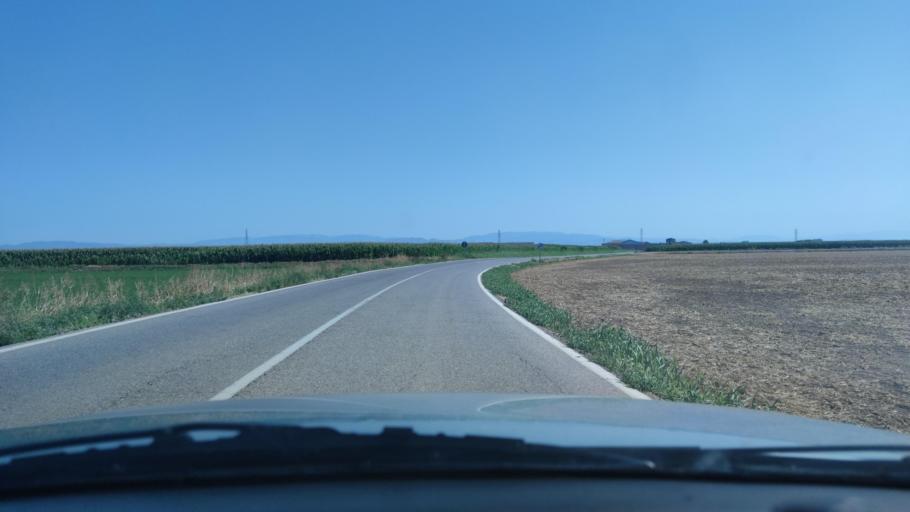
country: ES
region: Catalonia
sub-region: Provincia de Lleida
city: Bellvis
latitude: 41.6428
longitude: 0.7947
